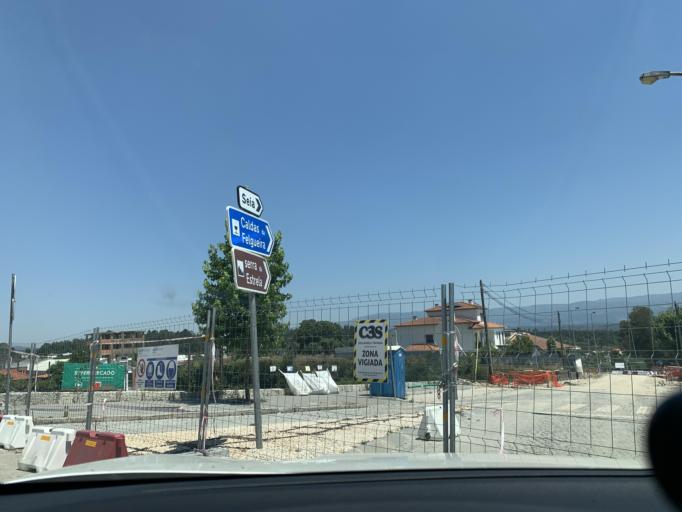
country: PT
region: Viseu
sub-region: Nelas
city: Nelas
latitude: 40.5287
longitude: -7.8532
